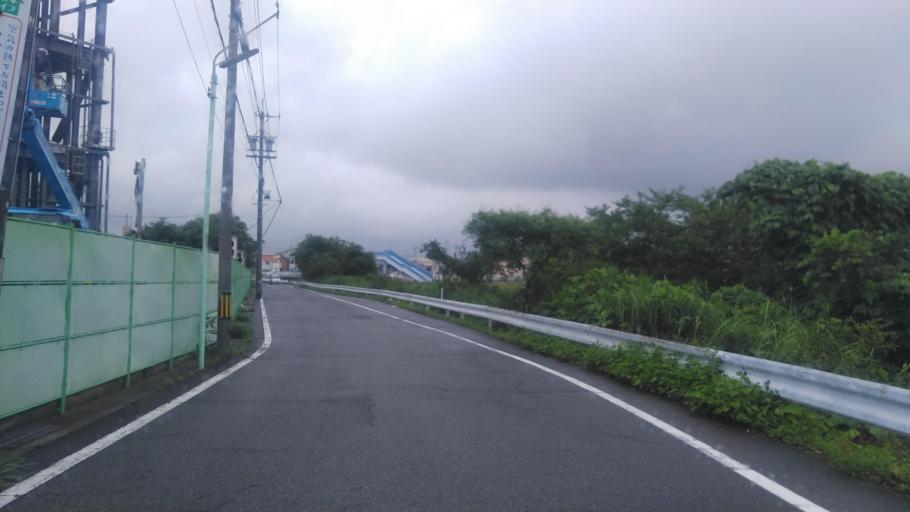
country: JP
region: Aichi
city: Kasugai
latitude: 35.2507
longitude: 137.0329
